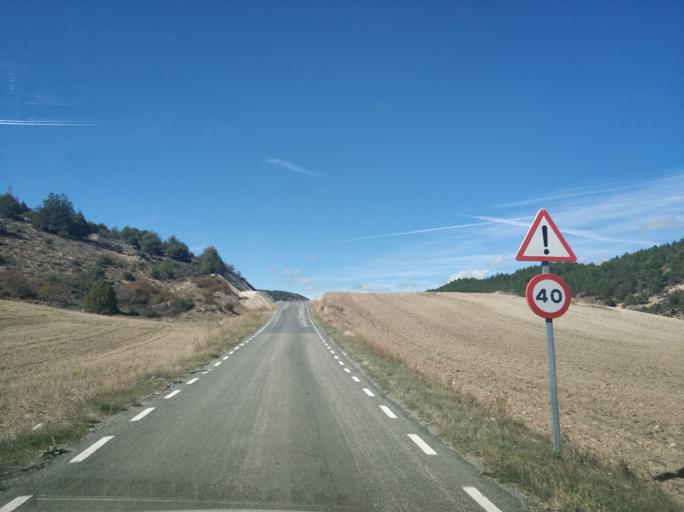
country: ES
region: Castille and Leon
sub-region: Provincia de Soria
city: Espeja de San Marcelino
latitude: 41.8133
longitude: -3.2266
